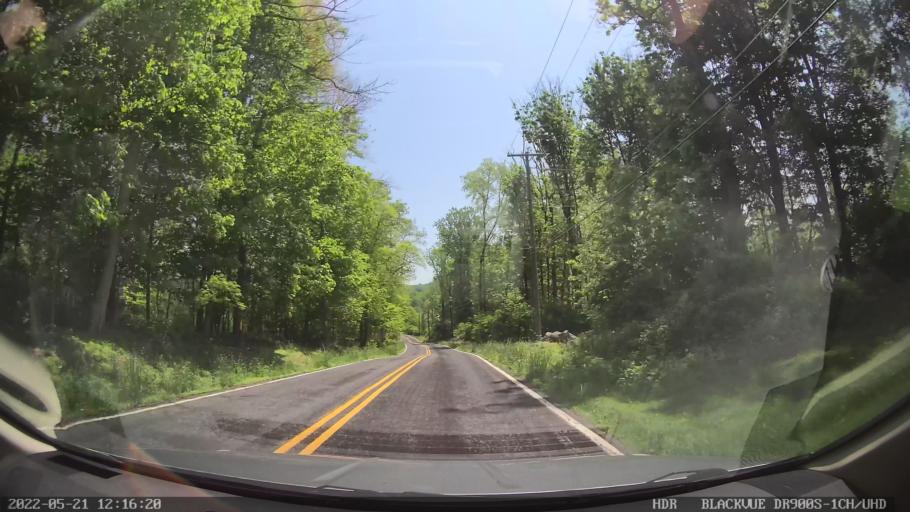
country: US
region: Pennsylvania
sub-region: Berks County
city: Red Lion
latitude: 40.4261
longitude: -75.6578
